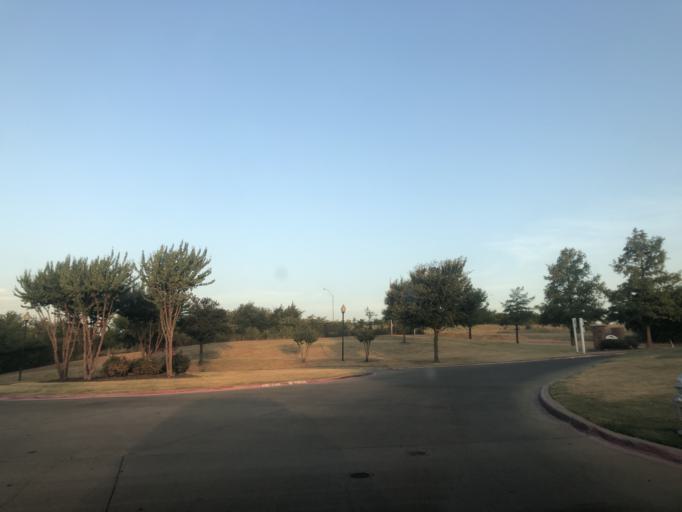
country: US
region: Texas
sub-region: Tarrant County
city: Sansom Park
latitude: 32.8050
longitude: -97.4186
